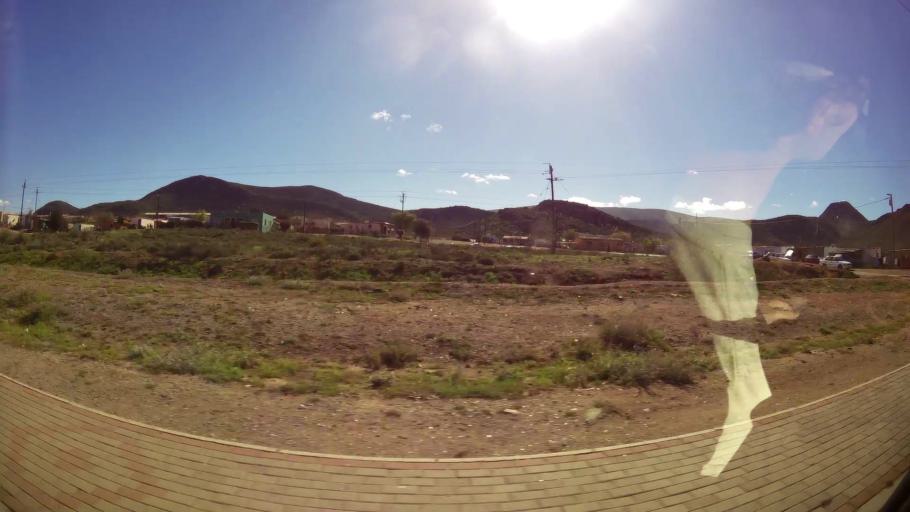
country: ZA
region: Western Cape
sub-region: Cape Winelands District Municipality
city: Ashton
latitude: -33.7689
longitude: 20.1493
